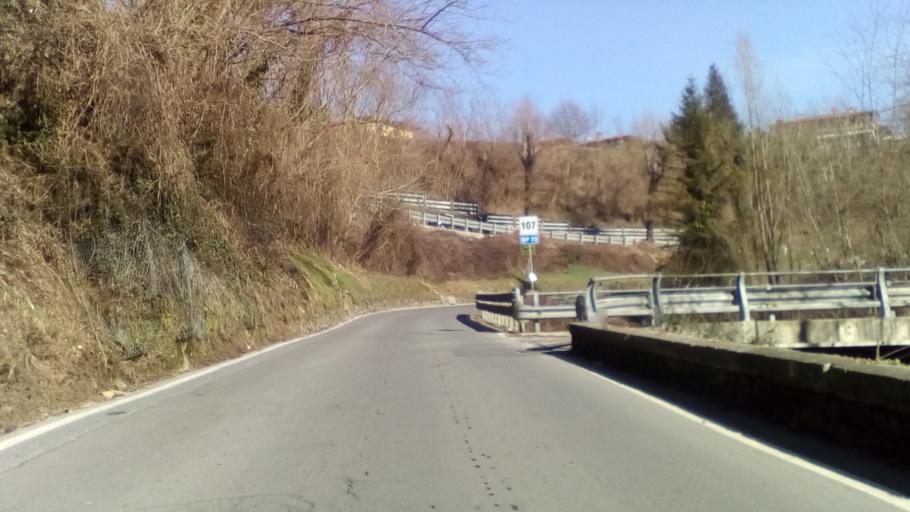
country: IT
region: Tuscany
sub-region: Provincia di Lucca
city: Castelnuovo di Garfagnana
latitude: 44.1191
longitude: 10.4112
